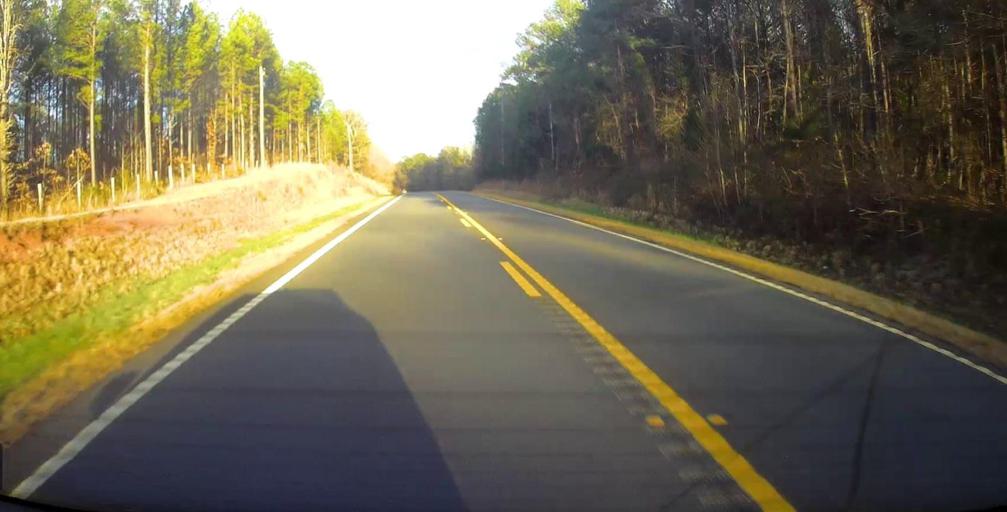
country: US
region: Georgia
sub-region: Talbot County
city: Sardis
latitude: 32.7480
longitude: -84.5855
